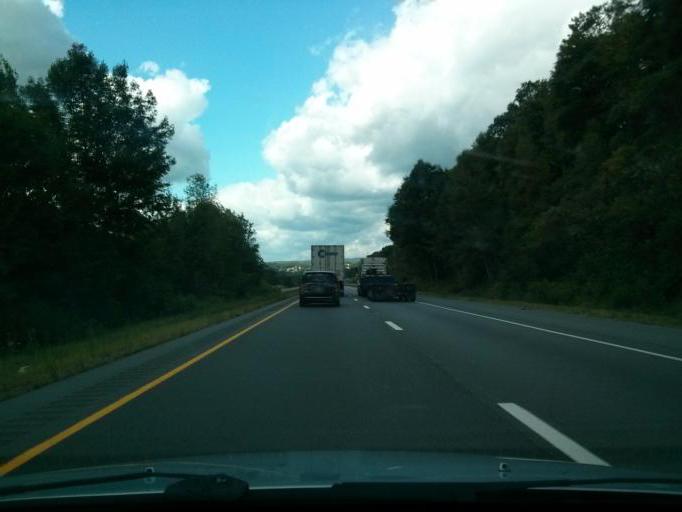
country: US
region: Pennsylvania
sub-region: Clearfield County
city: DuBois
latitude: 41.1455
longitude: -78.7638
